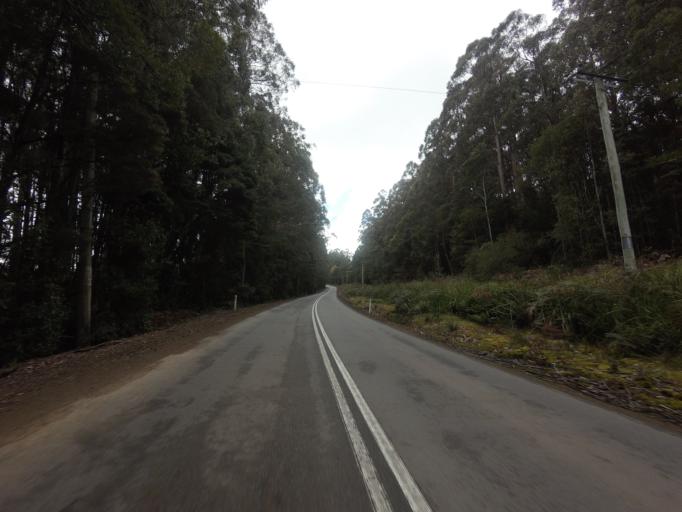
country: AU
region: Tasmania
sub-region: Huon Valley
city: Geeveston
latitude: -43.3851
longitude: 146.9615
